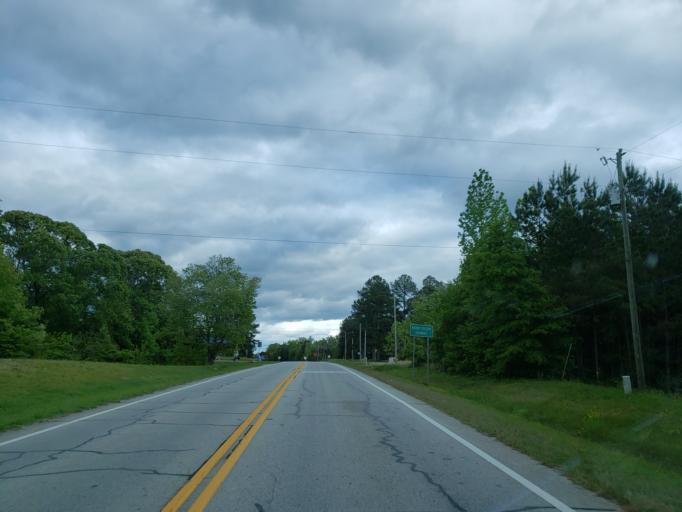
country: US
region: Georgia
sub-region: Haralson County
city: Buchanan
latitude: 33.8165
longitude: -85.1023
